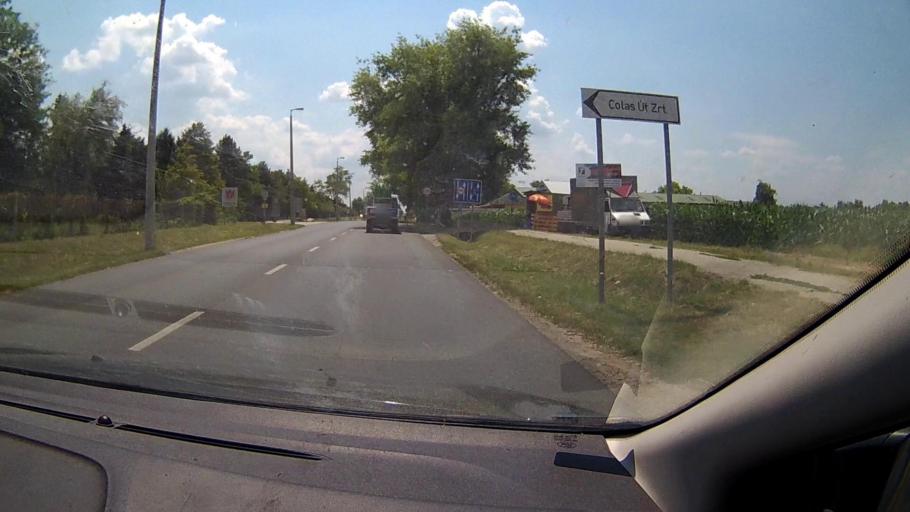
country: HU
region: Komarom-Esztergom
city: Tata
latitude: 47.6337
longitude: 18.3130
